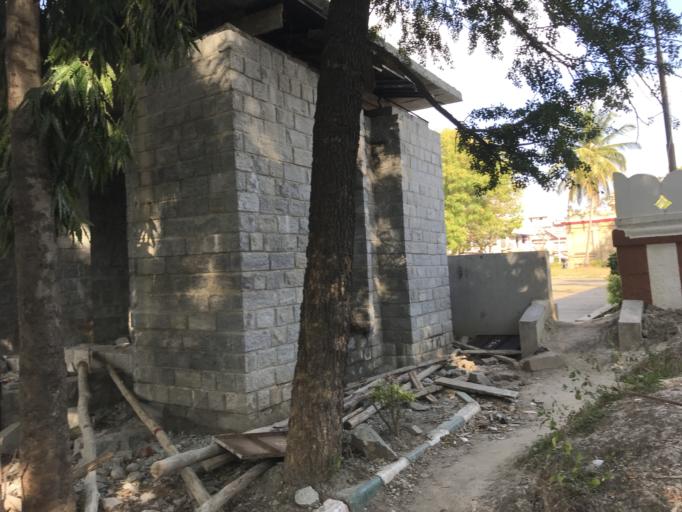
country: IN
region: Karnataka
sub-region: Hassan
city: Shravanabelagola
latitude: 12.8587
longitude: 76.4861
